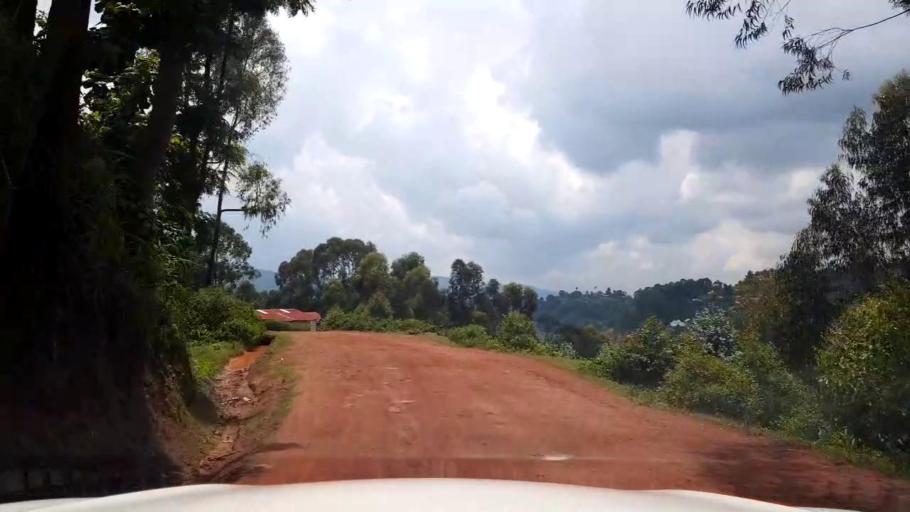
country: UG
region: Western Region
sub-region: Kisoro District
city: Kisoro
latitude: -1.4185
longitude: 29.8291
